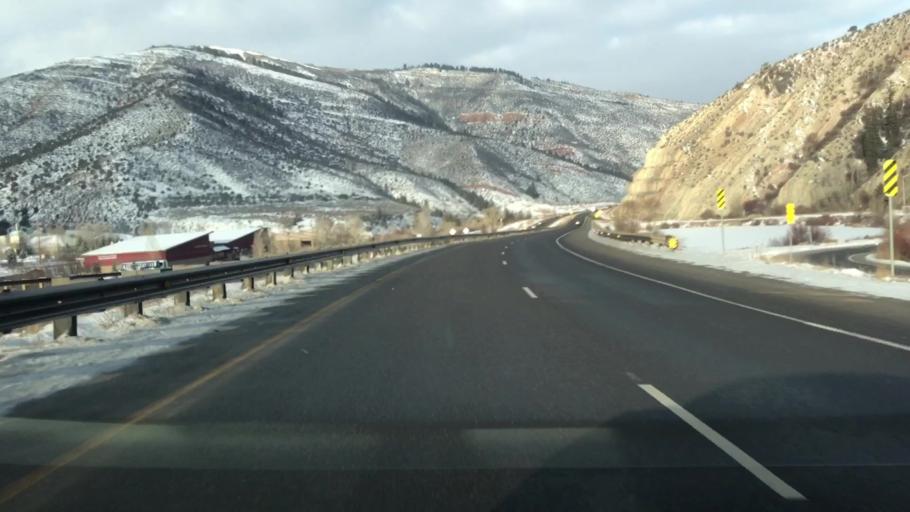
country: US
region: Colorado
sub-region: Eagle County
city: Edwards
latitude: 39.6560
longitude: -106.6327
